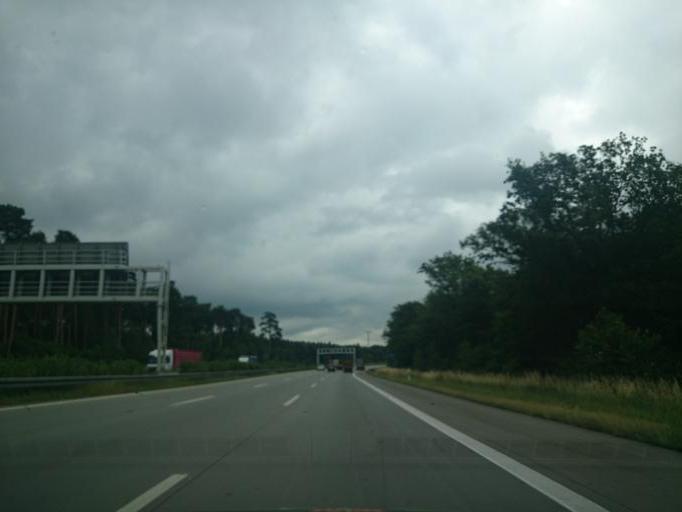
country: DE
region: Brandenburg
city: Schulzendorf
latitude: 52.3196
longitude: 13.5794
